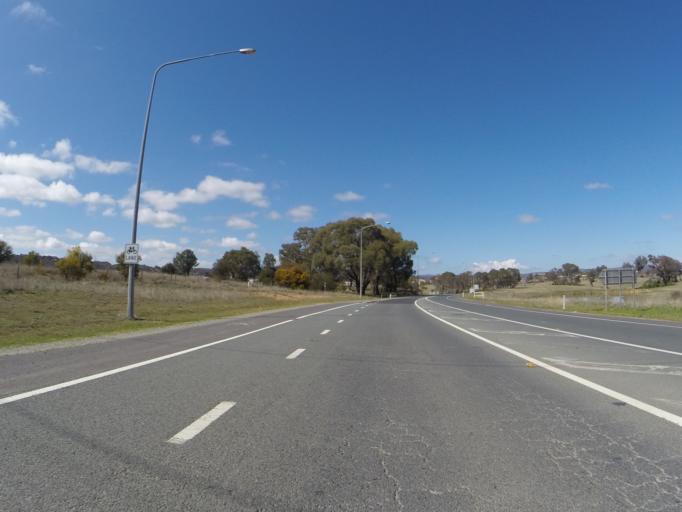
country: AU
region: New South Wales
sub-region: Queanbeyan
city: Queanbeyan
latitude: -35.3314
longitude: 149.2381
